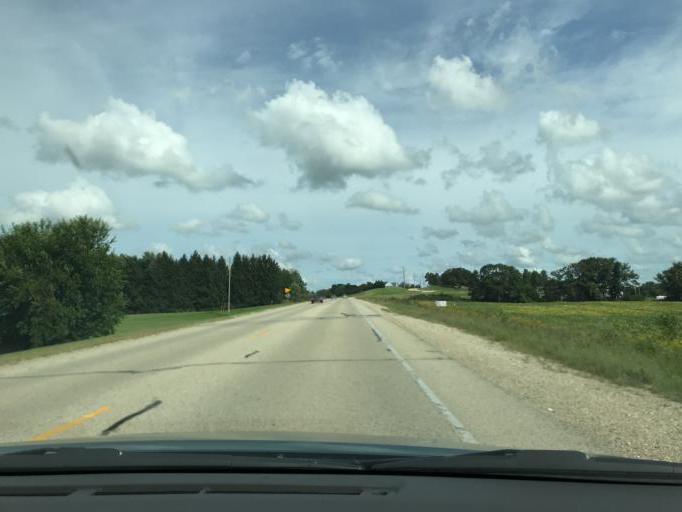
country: US
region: Wisconsin
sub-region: Racine County
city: Bohners Lake
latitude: 42.5978
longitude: -88.2223
